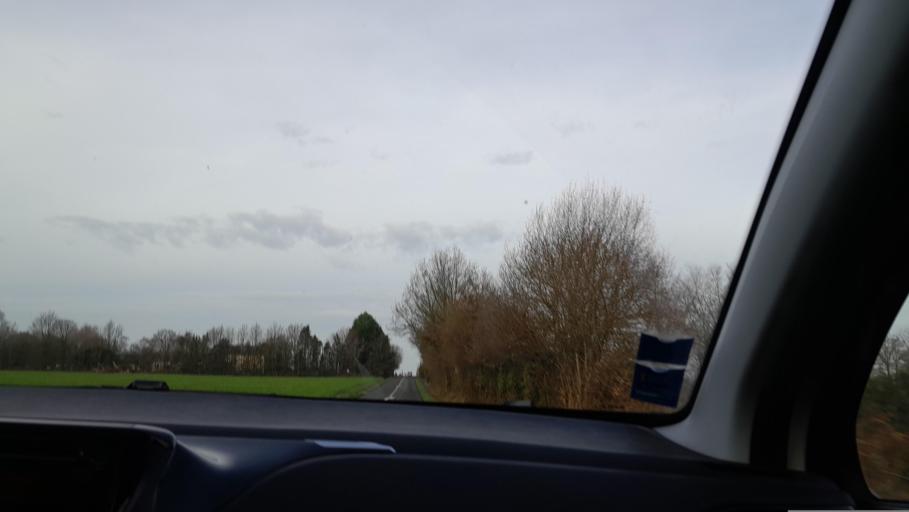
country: FR
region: Pays de la Loire
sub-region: Departement de la Mayenne
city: Ballots
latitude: 47.8872
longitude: -1.0323
